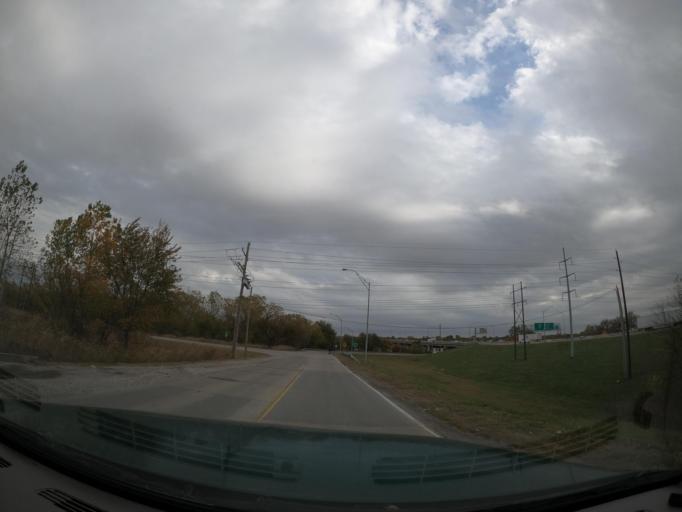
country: US
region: Oklahoma
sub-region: Tulsa County
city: Tulsa
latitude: 36.0908
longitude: -95.9943
